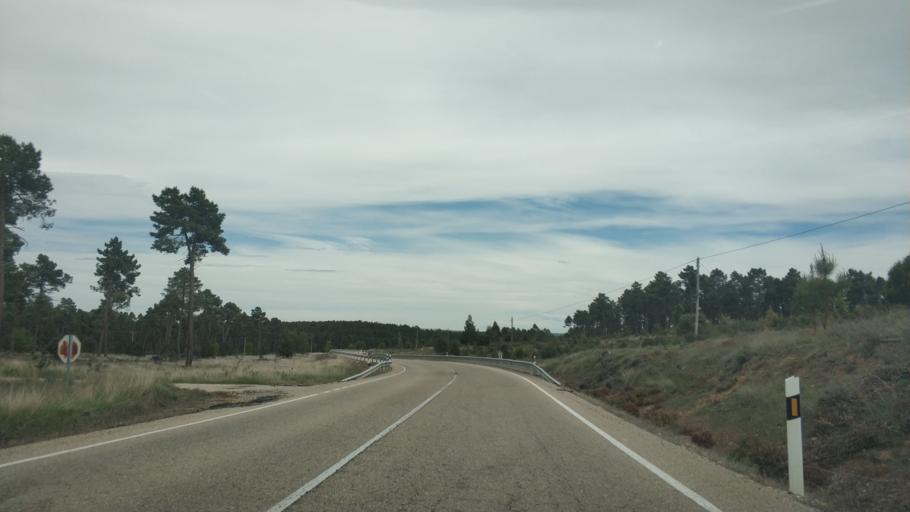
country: ES
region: Castille and Leon
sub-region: Provincia de Soria
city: Bayubas de Abajo
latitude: 41.5214
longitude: -2.9346
